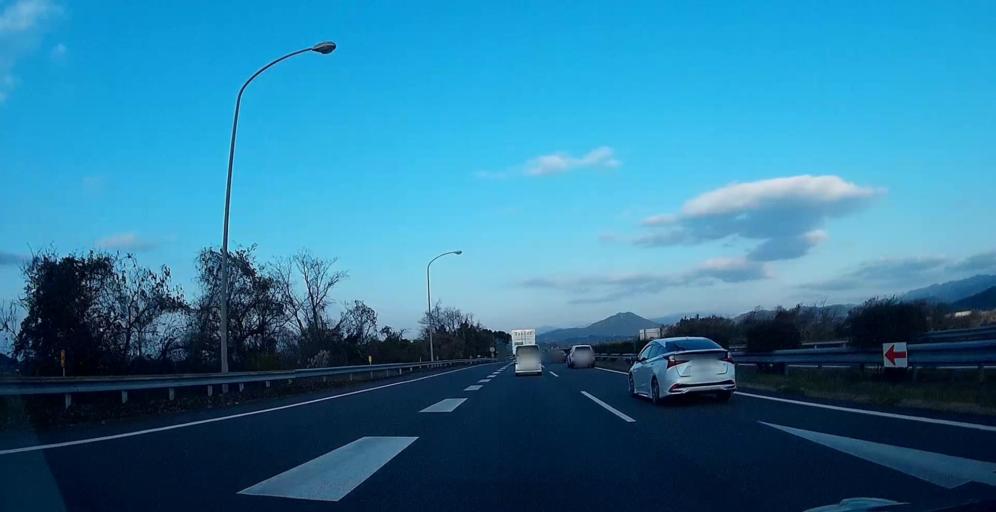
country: JP
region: Kumamoto
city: Uto
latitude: 32.7102
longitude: 130.7587
